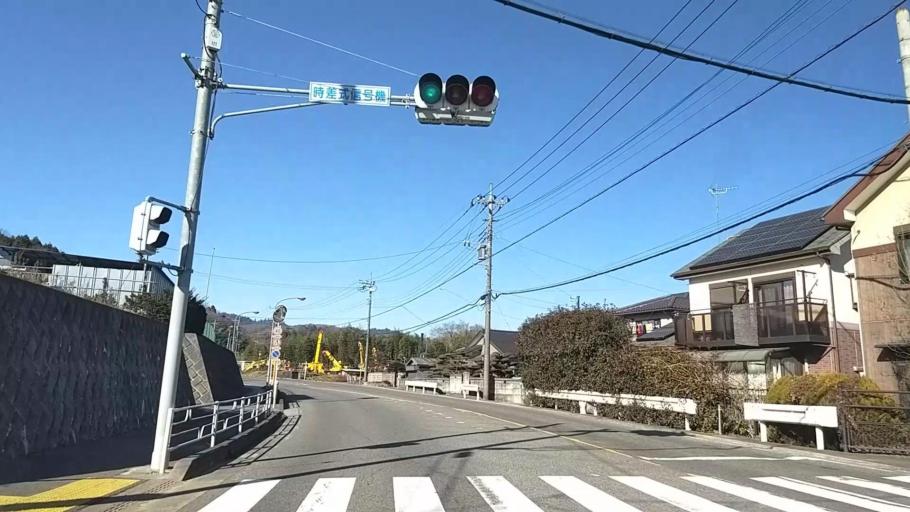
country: JP
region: Tokyo
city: Hachioji
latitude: 35.6096
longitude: 139.2945
